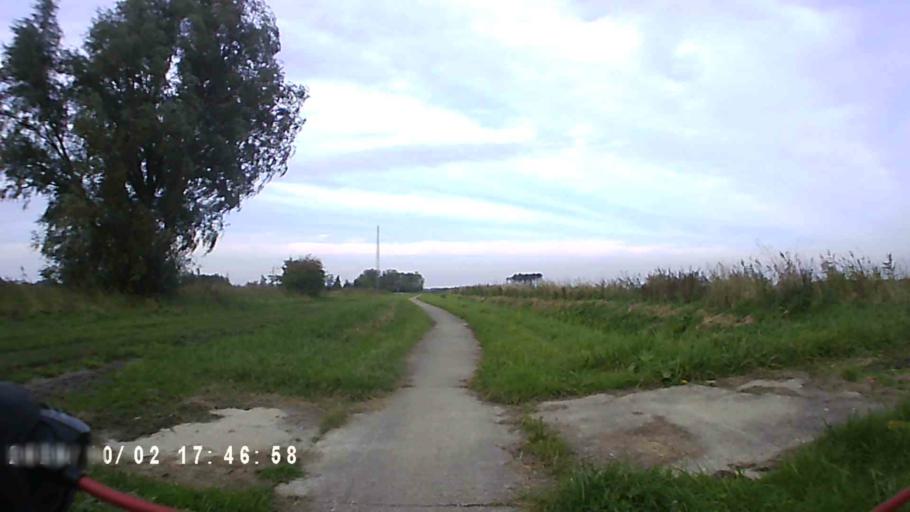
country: NL
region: Groningen
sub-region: Gemeente Zuidhorn
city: Oldehove
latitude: 53.3360
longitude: 6.3970
